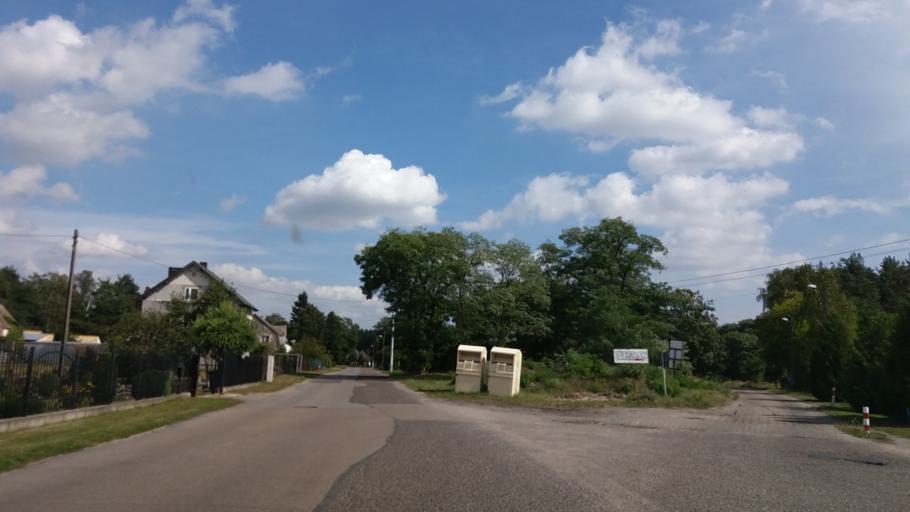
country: PL
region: West Pomeranian Voivodeship
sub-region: Powiat stargardzki
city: Kobylanka
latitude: 53.3654
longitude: 14.8733
